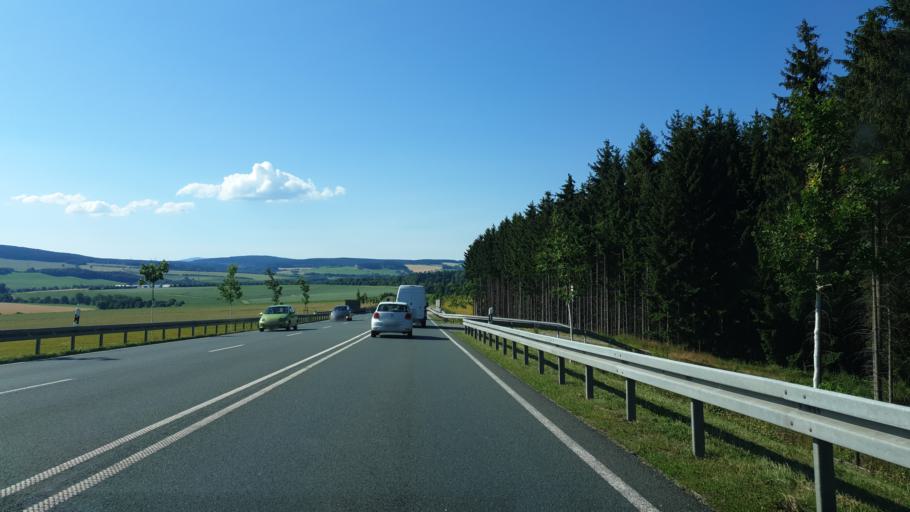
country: DE
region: Saxony
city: Dorfchemnitz
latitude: 50.6682
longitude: 12.8083
